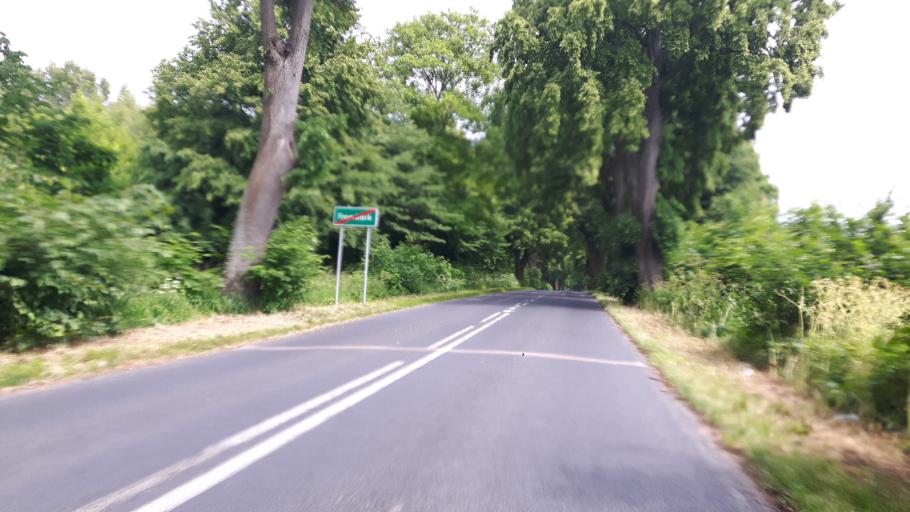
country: PL
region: Warmian-Masurian Voivodeship
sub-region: Powiat braniewski
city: Frombork
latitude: 54.3585
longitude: 19.7026
